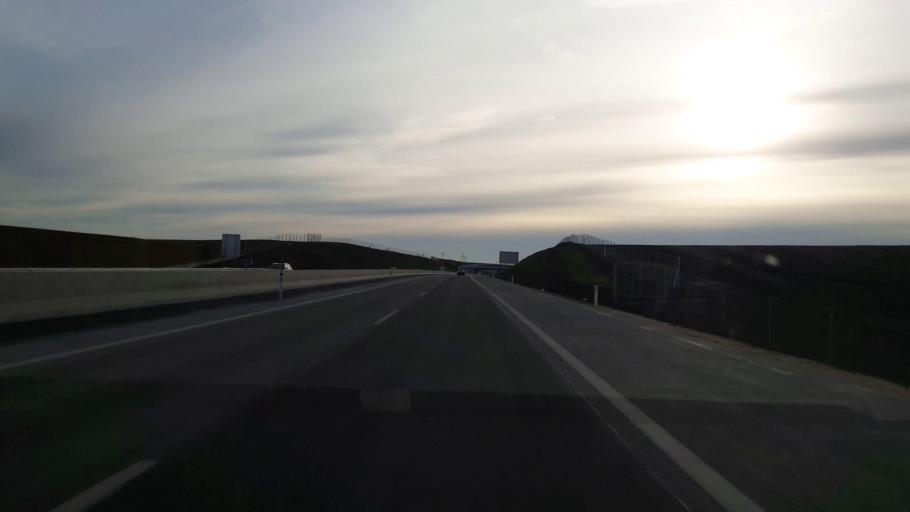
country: AT
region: Lower Austria
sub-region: Politischer Bezirk Mistelbach
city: Wilfersdorf
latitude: 48.5905
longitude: 16.6290
